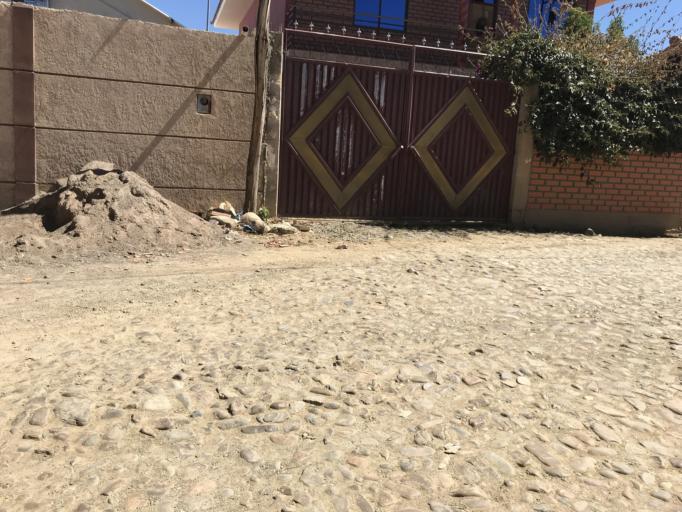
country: BO
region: Cochabamba
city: Tarata
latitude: -17.6169
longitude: -66.0272
